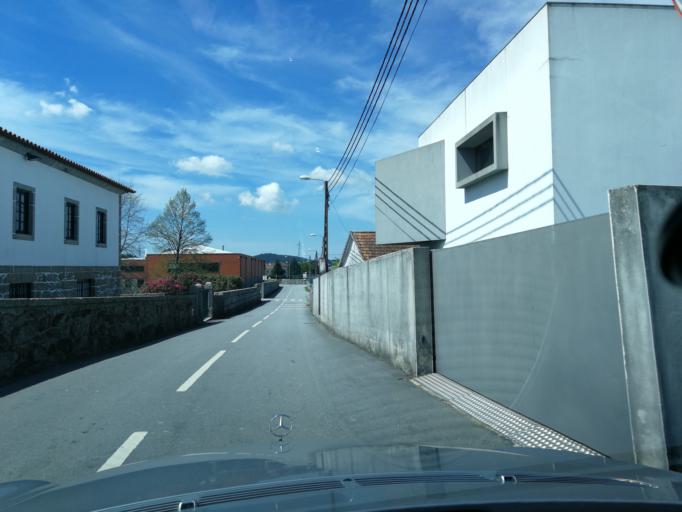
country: PT
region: Braga
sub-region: Vila Nova de Famalicao
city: Vila Nova de Famalicao
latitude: 41.4318
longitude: -8.5315
